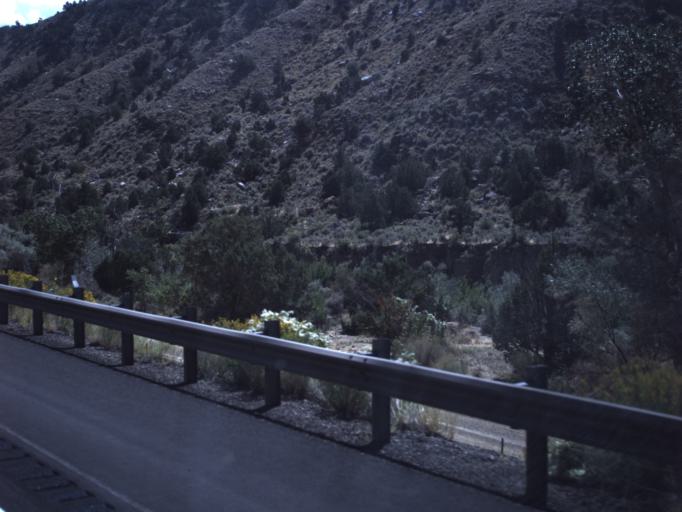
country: US
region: Utah
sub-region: Sevier County
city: Salina
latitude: 38.9035
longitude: -111.6800
